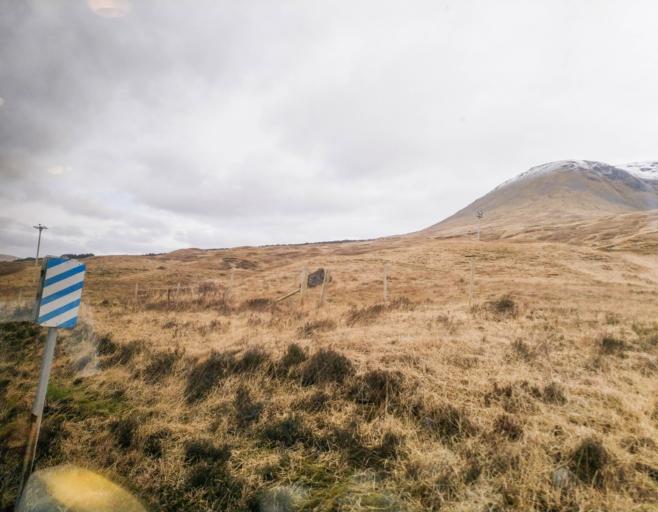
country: GB
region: Scotland
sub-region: Highland
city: Spean Bridge
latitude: 56.5121
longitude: -4.7611
